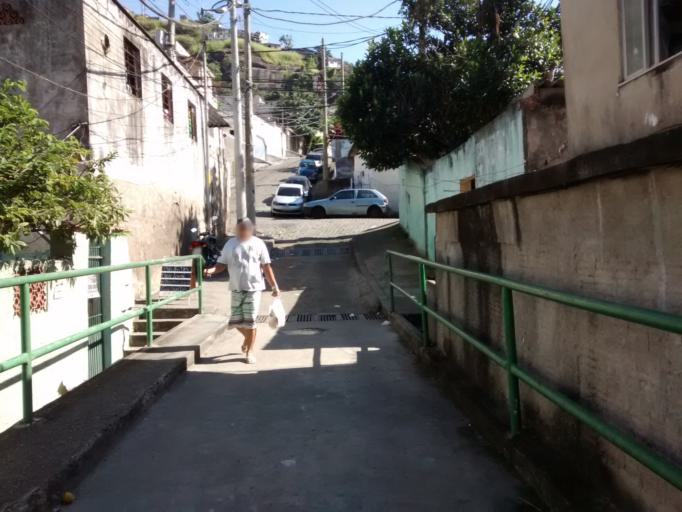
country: BR
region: Rio de Janeiro
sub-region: Rio De Janeiro
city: Rio de Janeiro
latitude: -22.9327
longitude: -43.2568
